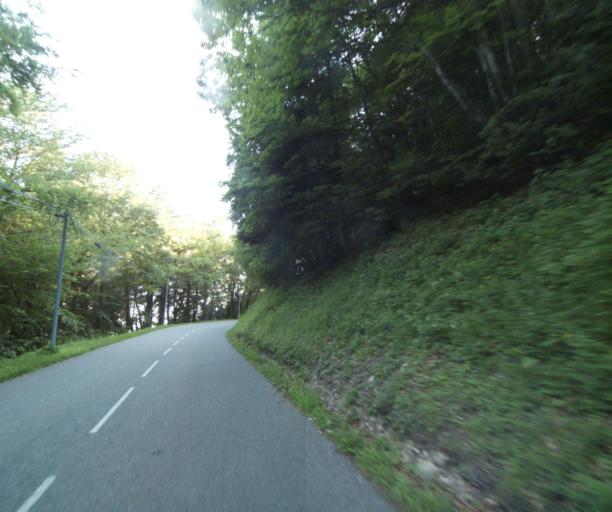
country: FR
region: Rhone-Alpes
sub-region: Departement de la Haute-Savoie
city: Lyaud
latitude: 46.3121
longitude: 6.4967
